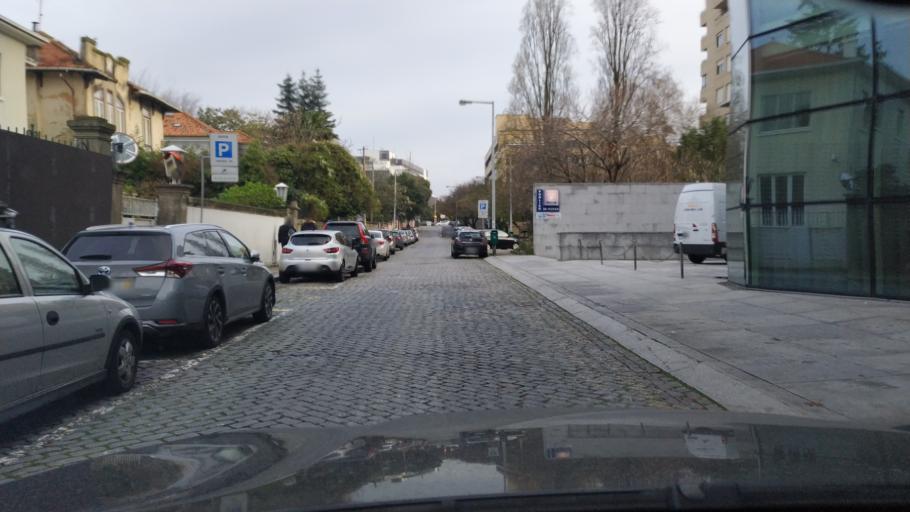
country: PT
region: Porto
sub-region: Matosinhos
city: Senhora da Hora
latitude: 41.1613
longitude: -8.6405
